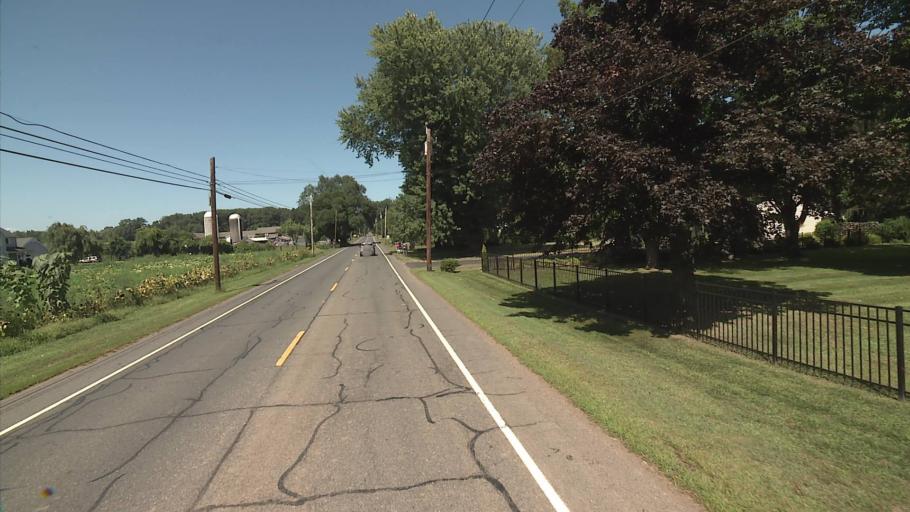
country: US
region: Connecticut
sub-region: Hartford County
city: Thompsonville
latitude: 42.0038
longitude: -72.6150
